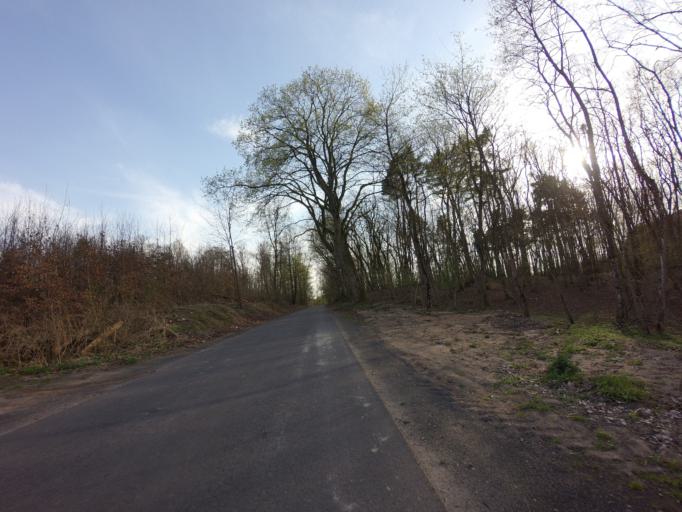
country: PL
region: West Pomeranian Voivodeship
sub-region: Powiat choszczenski
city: Choszczno
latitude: 53.1863
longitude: 15.5027
